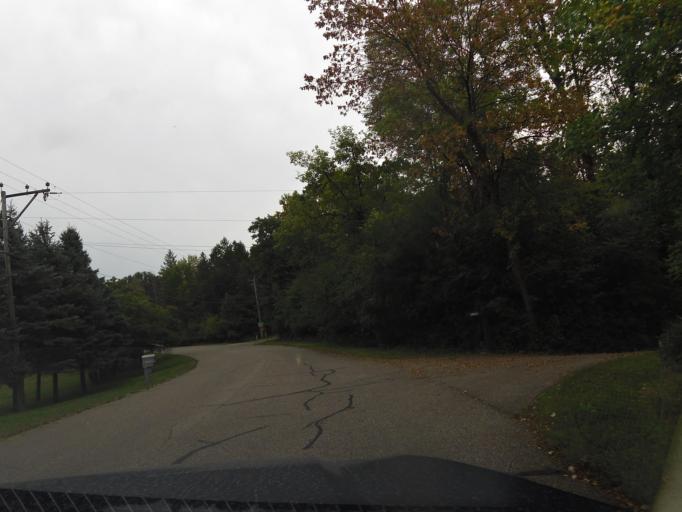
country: US
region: Minnesota
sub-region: Washington County
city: Afton
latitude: 44.8764
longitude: -92.8061
